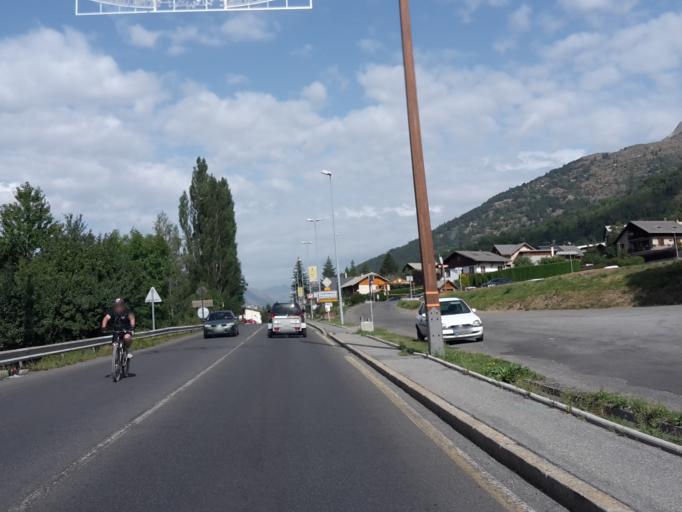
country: FR
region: Provence-Alpes-Cote d'Azur
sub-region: Departement des Hautes-Alpes
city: Saint-Chaffrey
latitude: 44.9310
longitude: 6.5927
